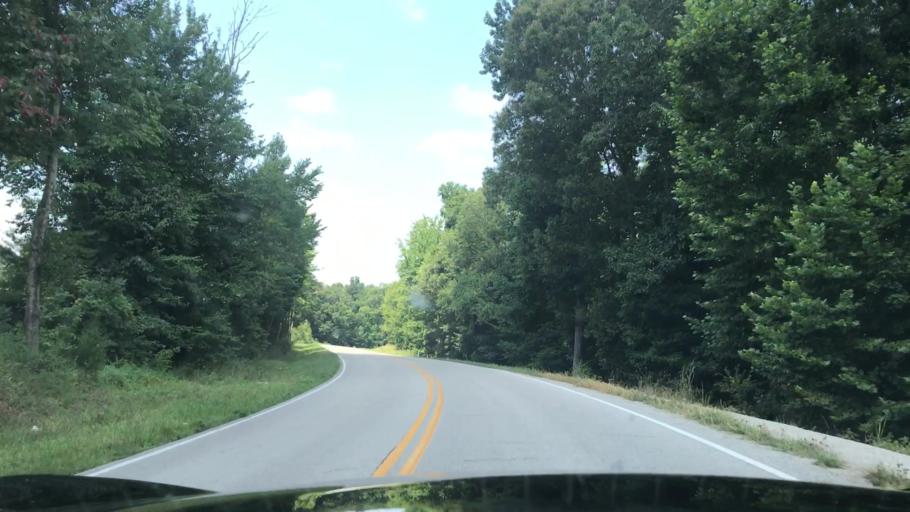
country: US
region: Kentucky
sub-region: Butler County
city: Morgantown
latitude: 37.1806
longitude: -86.8568
